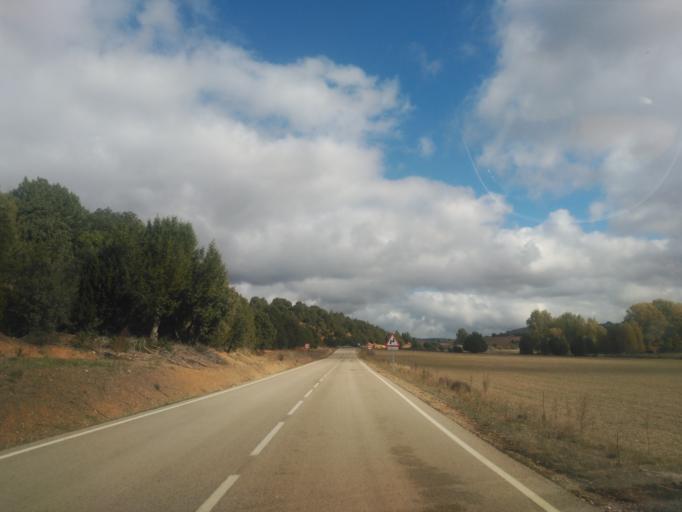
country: ES
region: Castille and Leon
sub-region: Provincia de Soria
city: Alcubilla de Avellaneda
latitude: 41.7409
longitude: -3.2923
